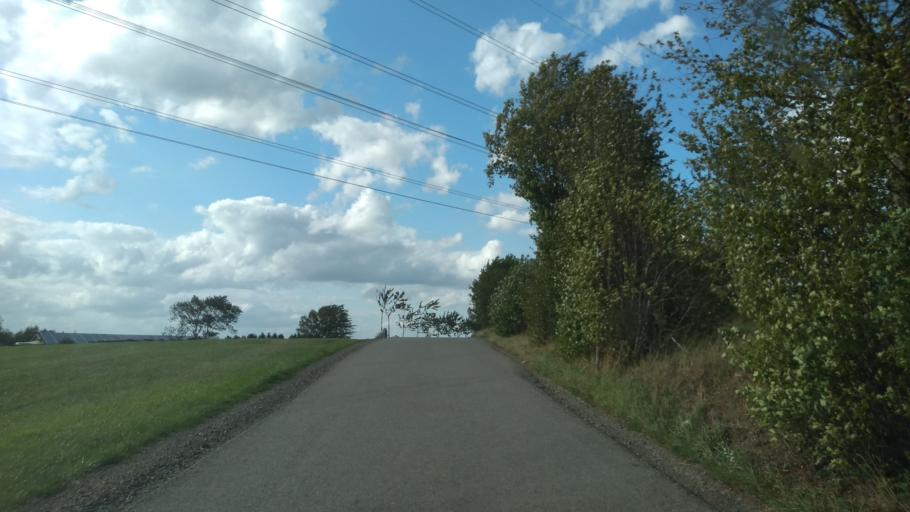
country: DE
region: North Rhine-Westphalia
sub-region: Regierungsbezirk Arnsberg
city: Schalksmuhle
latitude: 51.2162
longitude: 7.5488
